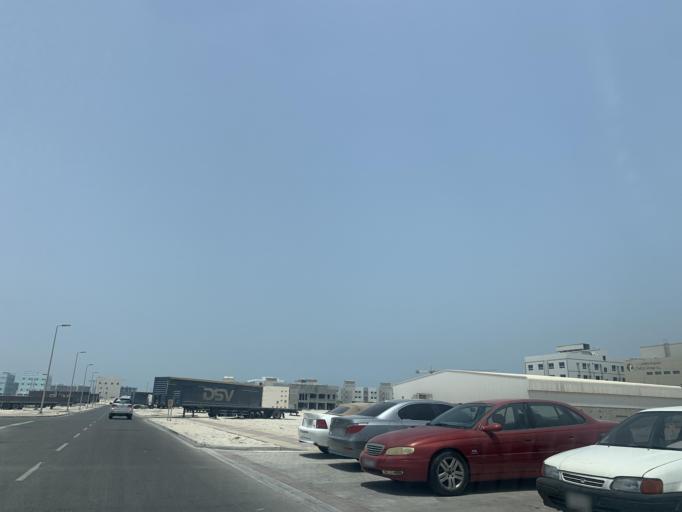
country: BH
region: Muharraq
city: Al Hadd
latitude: 26.2570
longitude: 50.6692
